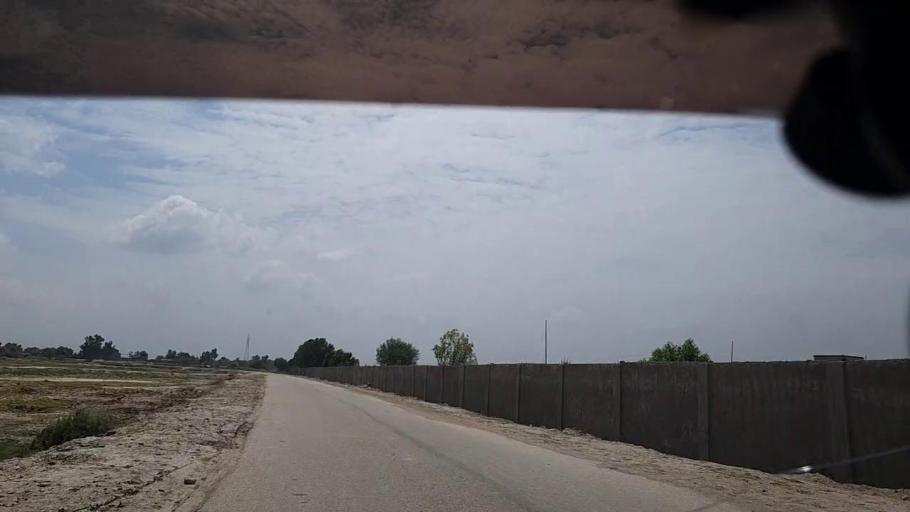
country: PK
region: Sindh
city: Ghauspur
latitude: 28.0928
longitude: 68.9596
